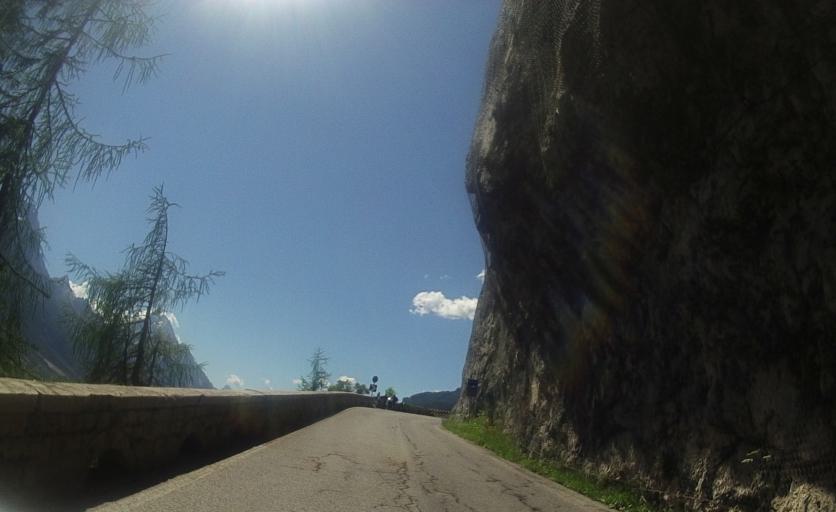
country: IT
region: Veneto
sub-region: Provincia di Belluno
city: Cortina d'Ampezzo
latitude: 46.5235
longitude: 12.1202
